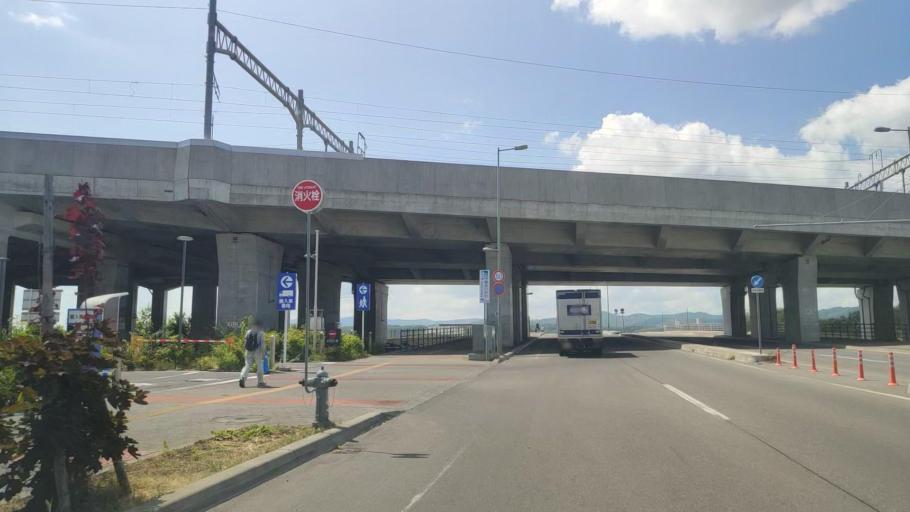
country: JP
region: Hokkaido
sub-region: Asahikawa-shi
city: Asahikawa
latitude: 43.7642
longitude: 142.3559
